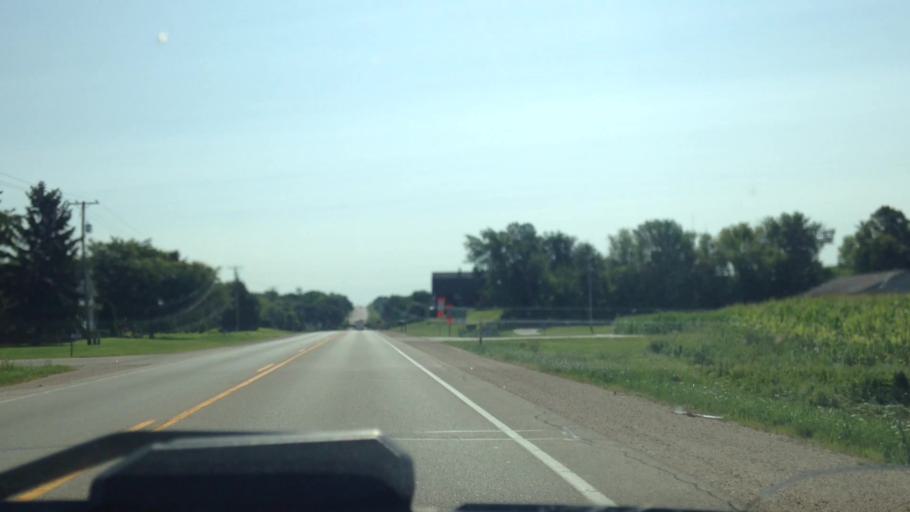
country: US
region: Wisconsin
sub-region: Dodge County
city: Mayville
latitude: 43.4429
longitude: -88.5493
